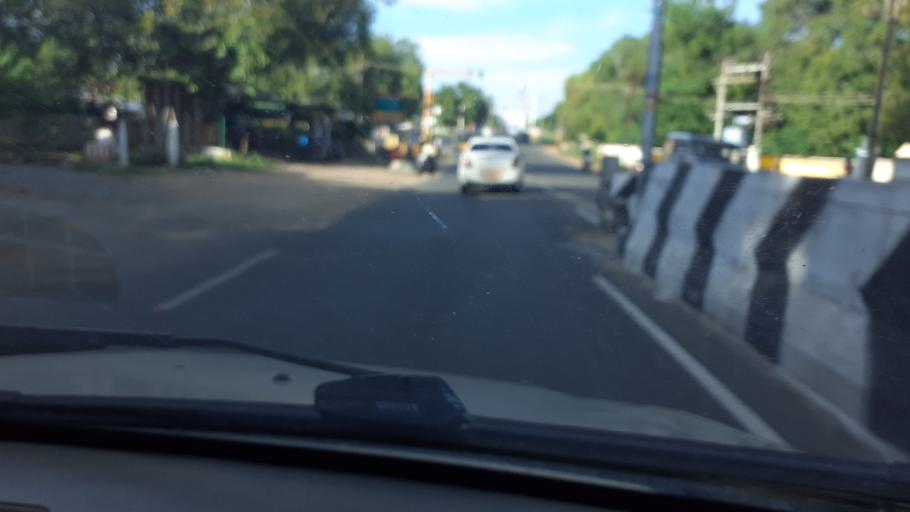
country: IN
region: Tamil Nadu
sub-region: Tirunelveli Kattabo
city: Tirunelveli
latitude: 8.7103
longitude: 77.7312
